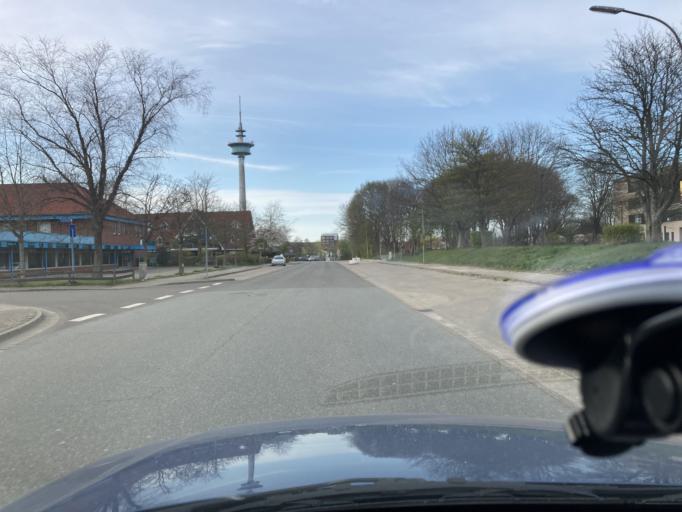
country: DE
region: Schleswig-Holstein
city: Heide
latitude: 54.2030
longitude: 9.1002
